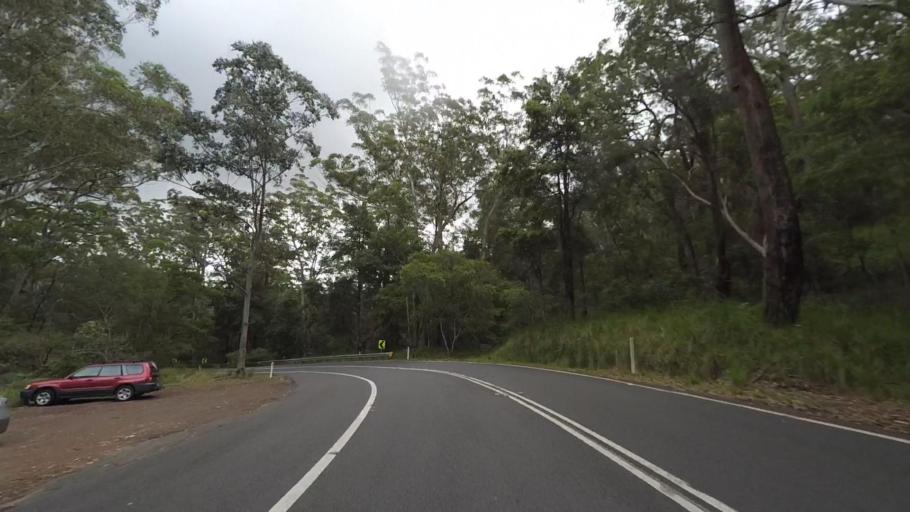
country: AU
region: New South Wales
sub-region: Wollongong
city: Helensburgh
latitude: -34.1487
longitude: 151.0301
